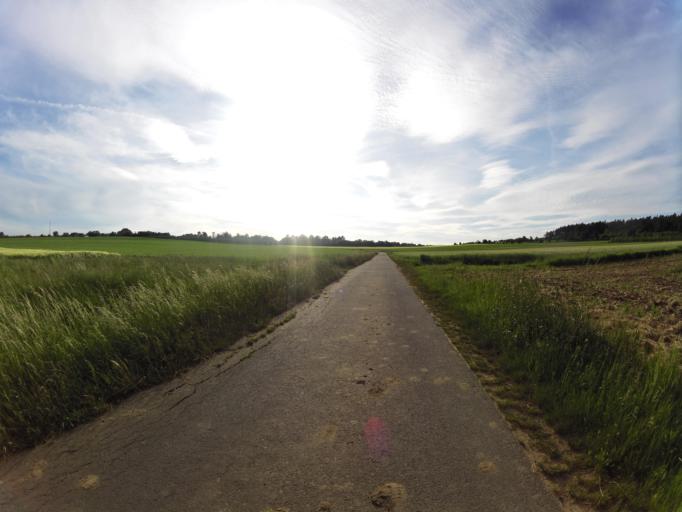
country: DE
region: Bavaria
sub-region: Regierungsbezirk Unterfranken
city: Sommerhausen
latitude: 49.6979
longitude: 10.0461
